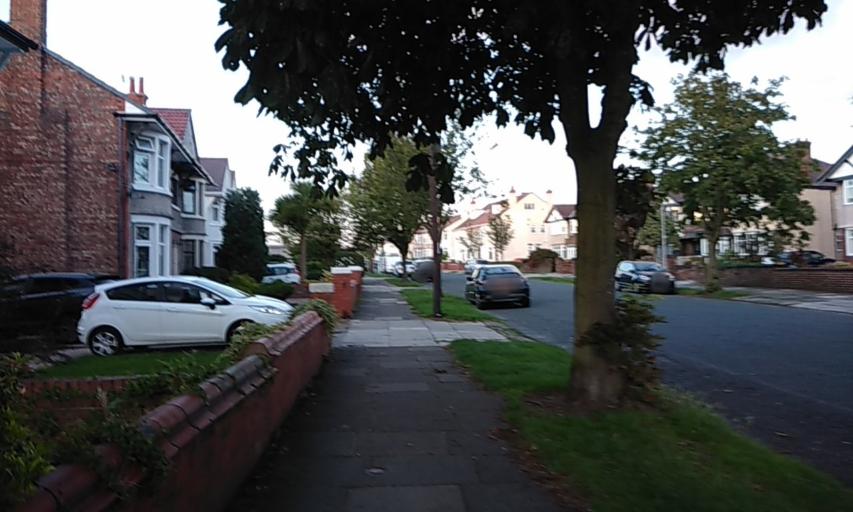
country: GB
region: England
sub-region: Metropolitan Borough of Wirral
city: Wallasey
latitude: 53.4234
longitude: -3.0561
